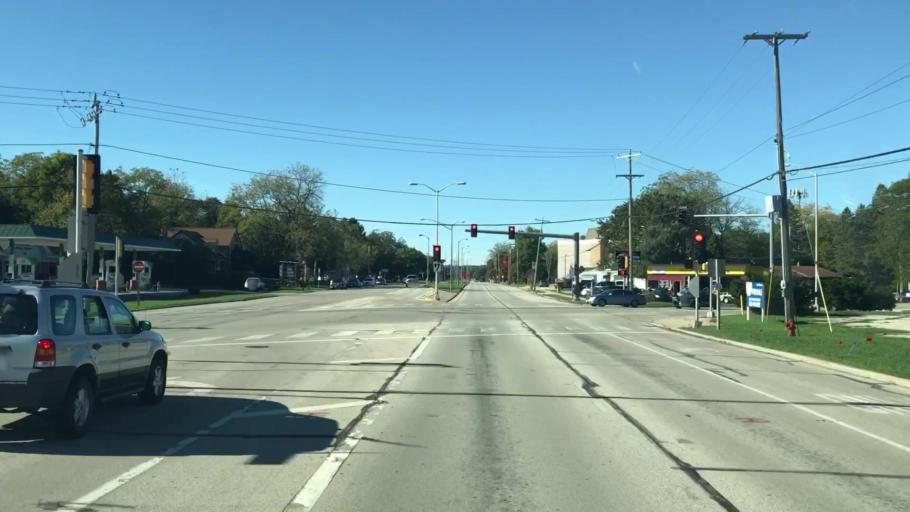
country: US
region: Wisconsin
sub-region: Milwaukee County
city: Hales Corners
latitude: 42.9450
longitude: -88.0360
